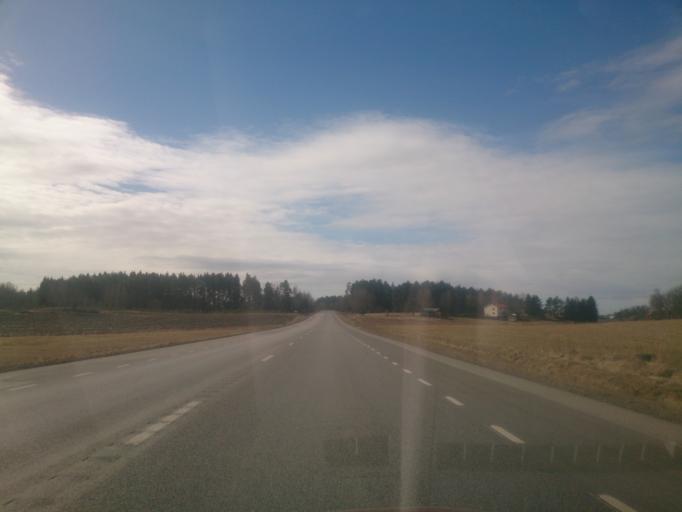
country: SE
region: OEstergoetland
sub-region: Norrkopings Kommun
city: Kimstad
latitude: 58.4982
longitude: 15.9656
